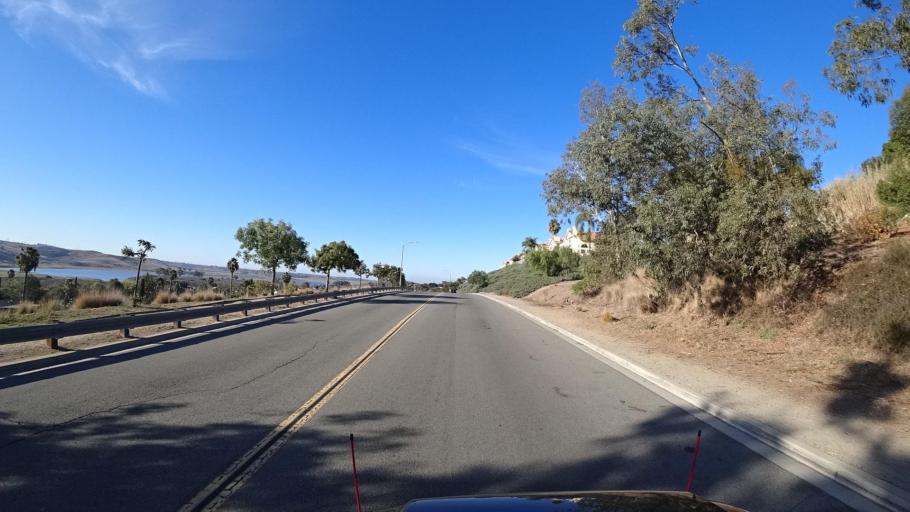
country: US
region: California
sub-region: San Diego County
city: La Presa
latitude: 32.7131
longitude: -116.9839
